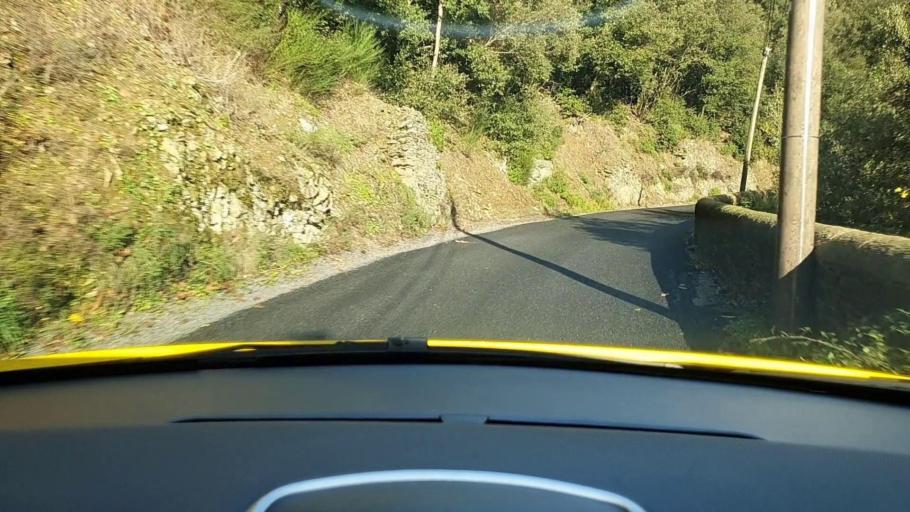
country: FR
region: Languedoc-Roussillon
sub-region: Departement du Gard
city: Sumene
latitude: 44.0212
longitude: 3.7294
